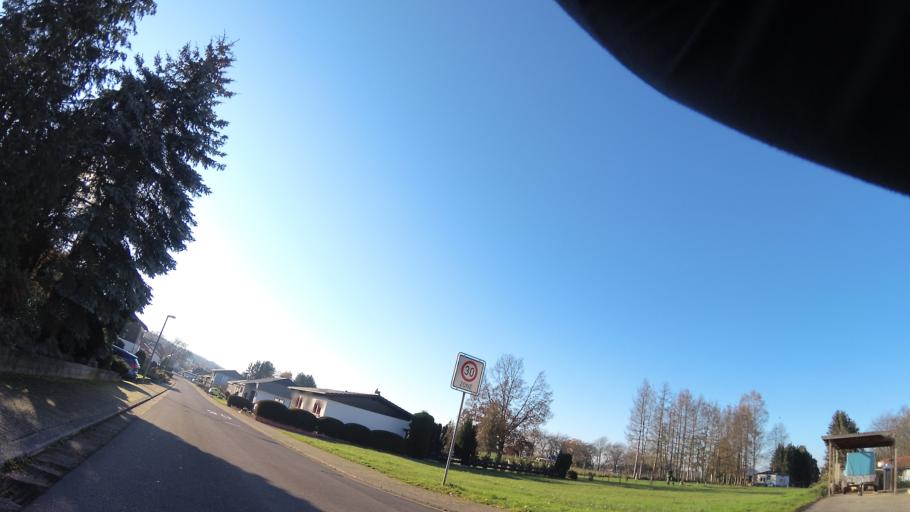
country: DE
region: Saarland
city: Schwalbach
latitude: 49.3007
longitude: 6.8276
